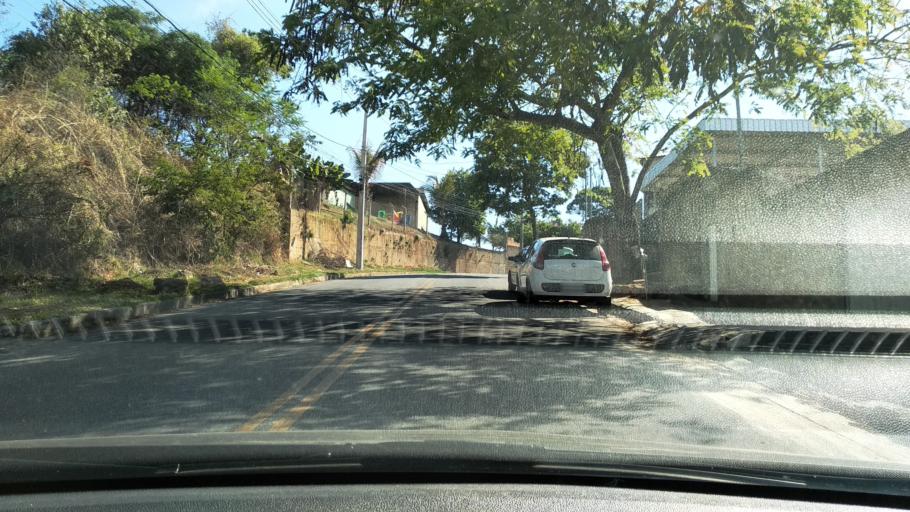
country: BR
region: Minas Gerais
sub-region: Belo Horizonte
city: Belo Horizonte
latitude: -19.8628
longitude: -43.8799
